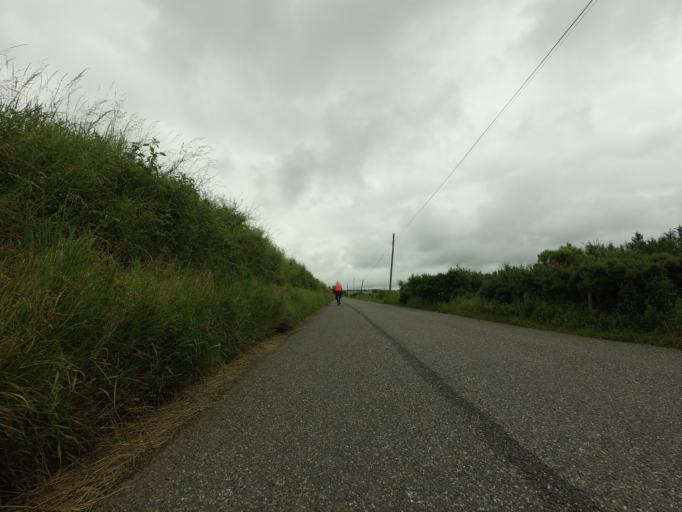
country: GB
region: Scotland
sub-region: Aberdeenshire
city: Turriff
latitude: 57.5361
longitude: -2.3731
